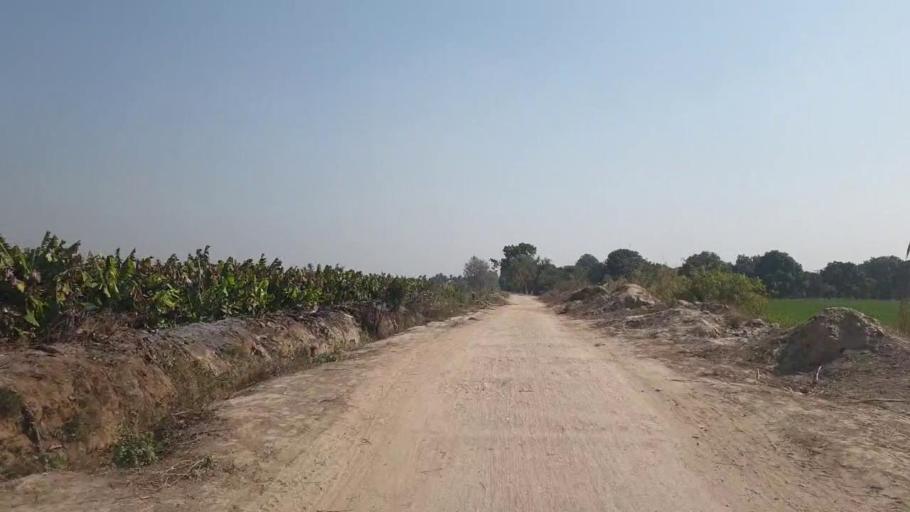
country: PK
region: Sindh
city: Tando Jam
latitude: 25.3409
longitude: 68.6087
